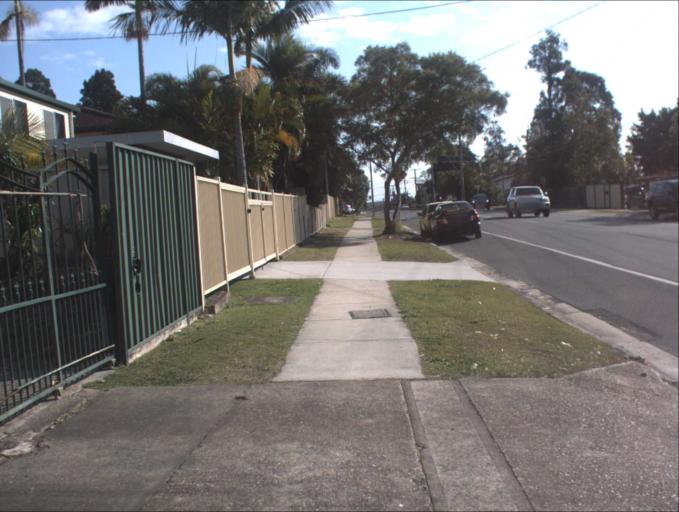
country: AU
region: Queensland
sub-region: Logan
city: Logan City
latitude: -27.6745
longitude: 153.0855
